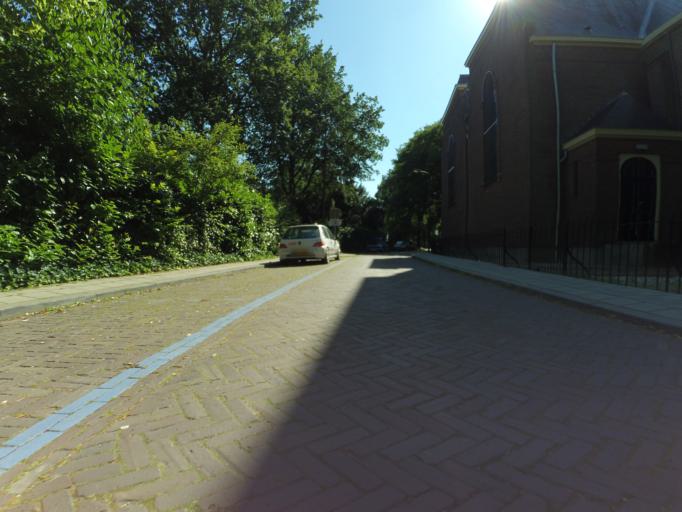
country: NL
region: Utrecht
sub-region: Gemeente Utrechtse Heuvelrug
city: Driebergen-Rijsenburg
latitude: 52.0550
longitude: 5.2760
